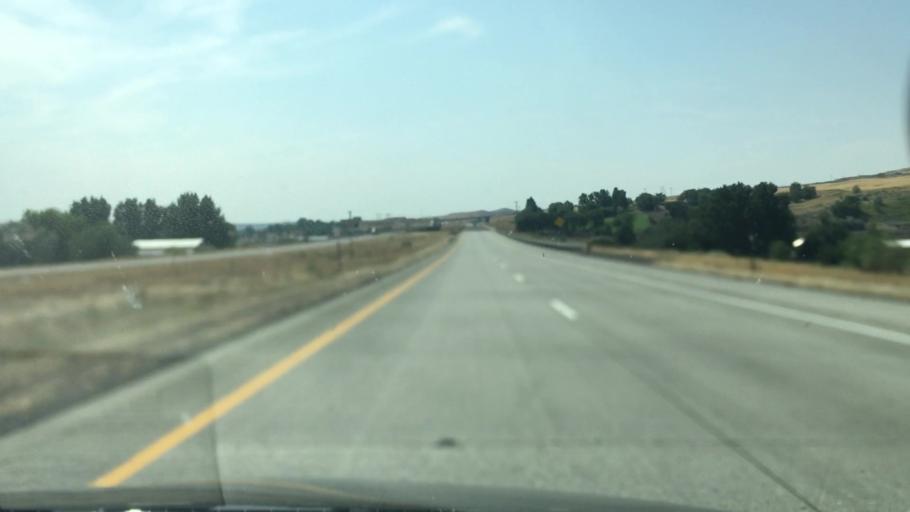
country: US
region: Idaho
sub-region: Elmore County
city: Glenns Ferry
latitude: 42.9611
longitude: -115.2738
